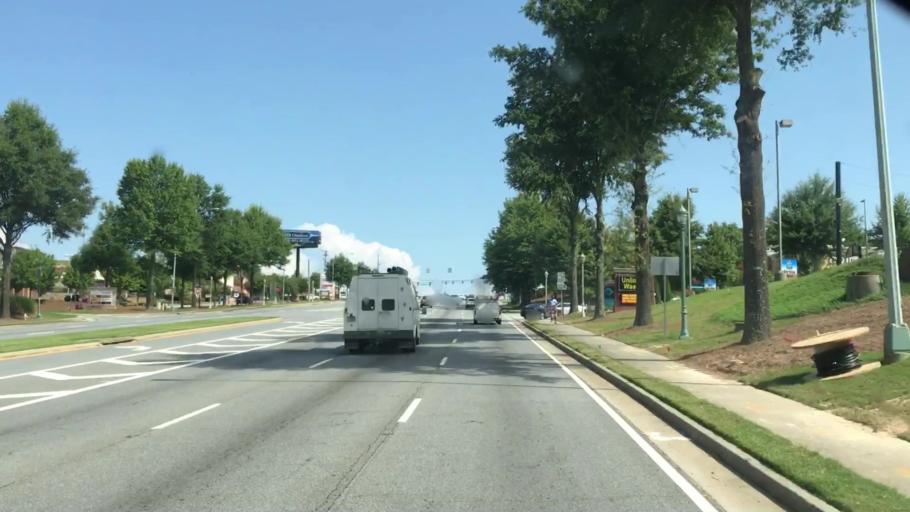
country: US
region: Georgia
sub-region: Gwinnett County
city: Buford
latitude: 34.0723
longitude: -83.9840
